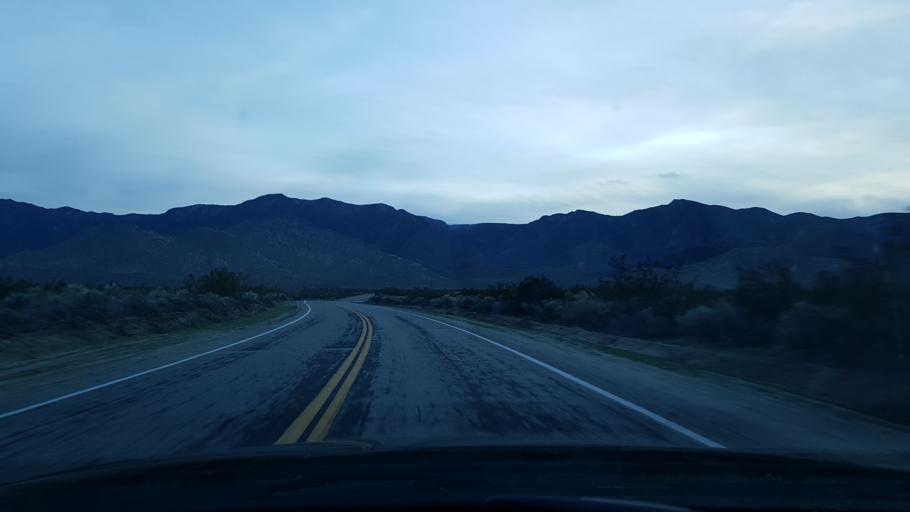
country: US
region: California
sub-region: San Diego County
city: Pine Valley
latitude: 32.9736
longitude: -116.3803
